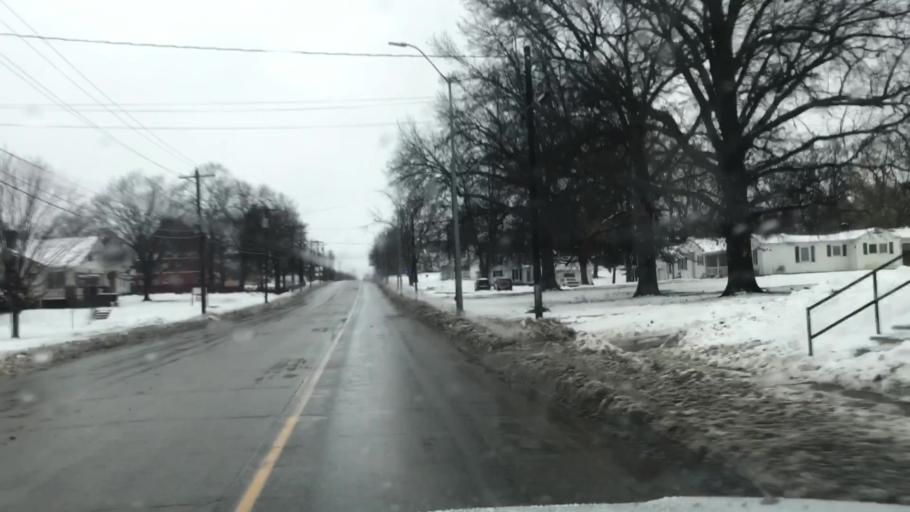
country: US
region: Missouri
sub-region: Clinton County
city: Cameron
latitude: 39.7359
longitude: -94.2361
